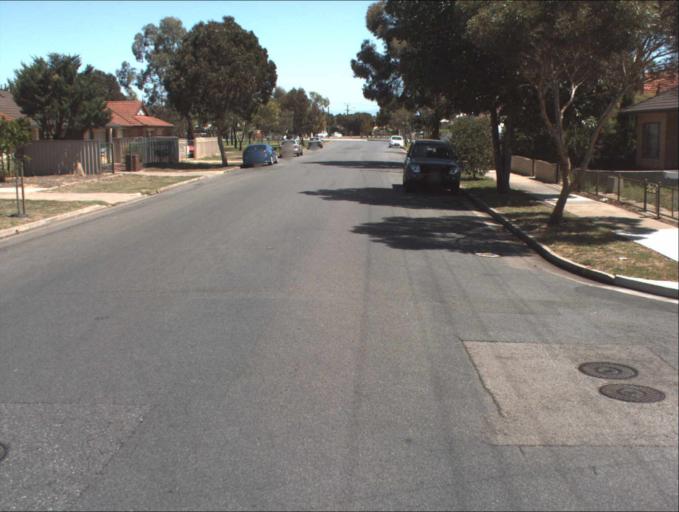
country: AU
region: South Australia
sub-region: Port Adelaide Enfield
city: Alberton
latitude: -34.8500
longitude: 138.5339
